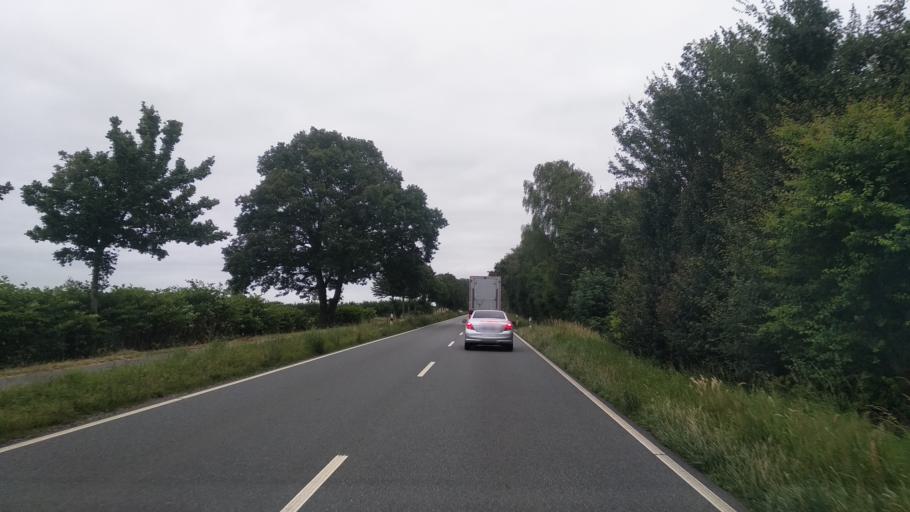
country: DE
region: Schleswig-Holstein
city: Ringsberg
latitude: 54.8034
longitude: 9.6102
